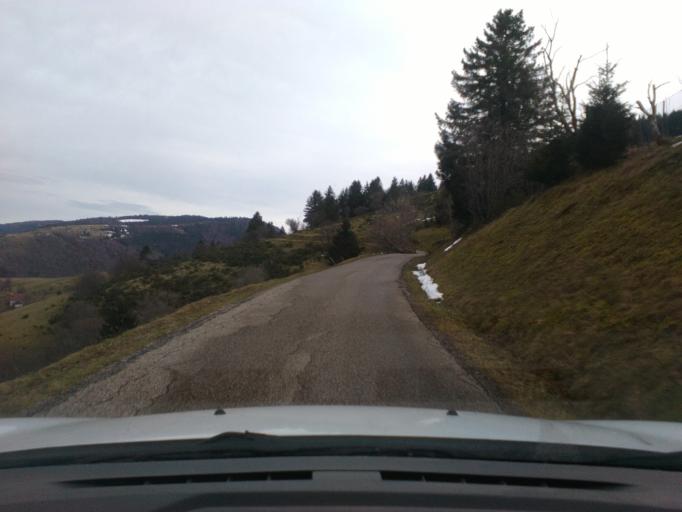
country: FR
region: Lorraine
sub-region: Departement des Vosges
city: La Bresse
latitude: 47.9934
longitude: 6.8746
